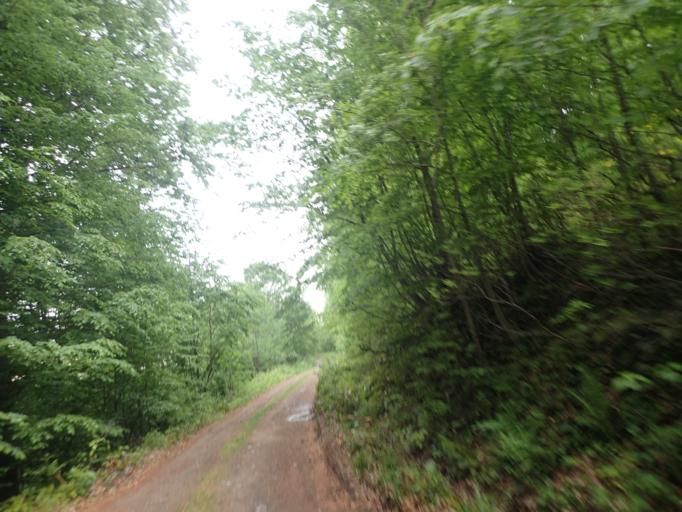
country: TR
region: Ordu
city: Akkus
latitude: 40.8707
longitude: 37.0860
